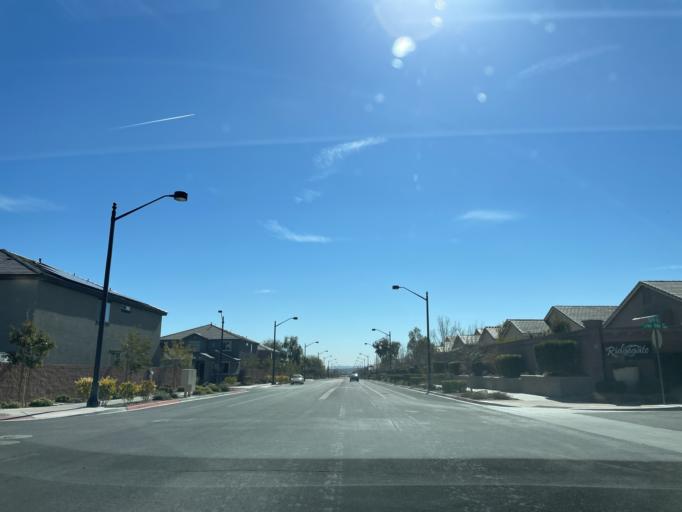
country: US
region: Nevada
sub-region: Clark County
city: Summerlin South
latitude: 36.2896
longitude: -115.3014
